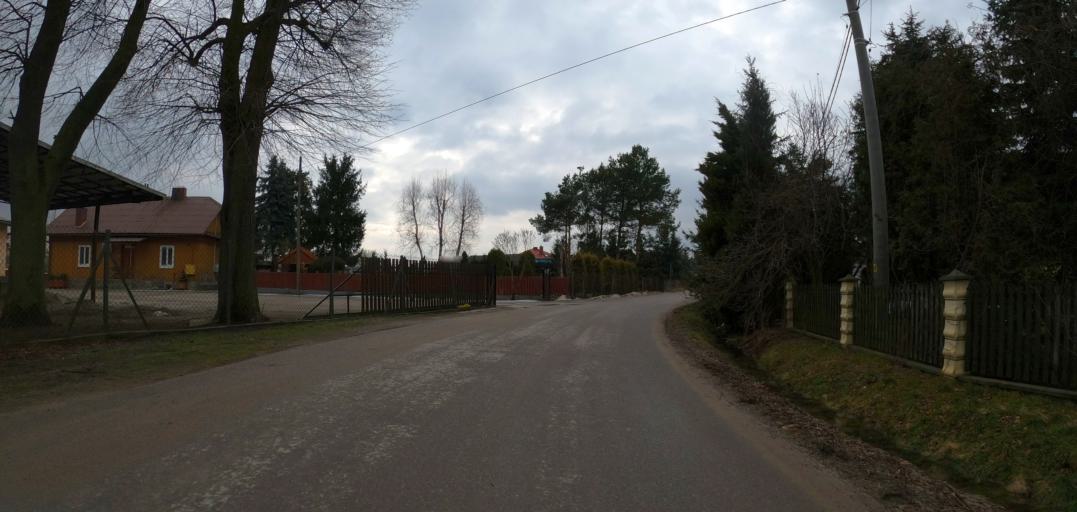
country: PL
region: Subcarpathian Voivodeship
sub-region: Powiat debicki
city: Pilzno
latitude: 49.9774
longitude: 21.3277
